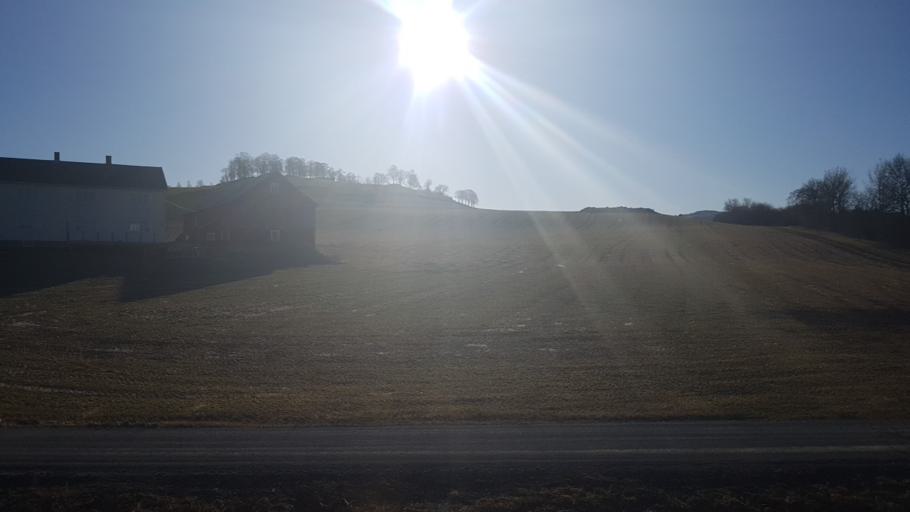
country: NO
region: Nord-Trondelag
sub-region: Levanger
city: Levanger
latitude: 63.7265
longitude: 11.2608
